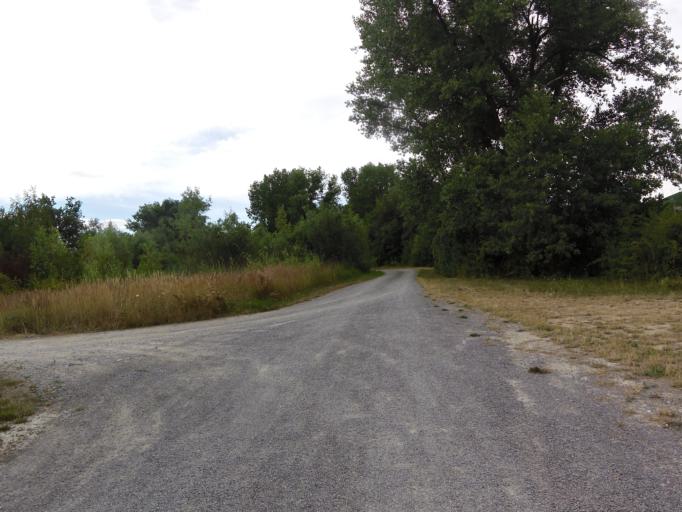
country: DE
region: Bavaria
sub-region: Regierungsbezirk Unterfranken
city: Randersacker
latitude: 49.7497
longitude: 9.9828
